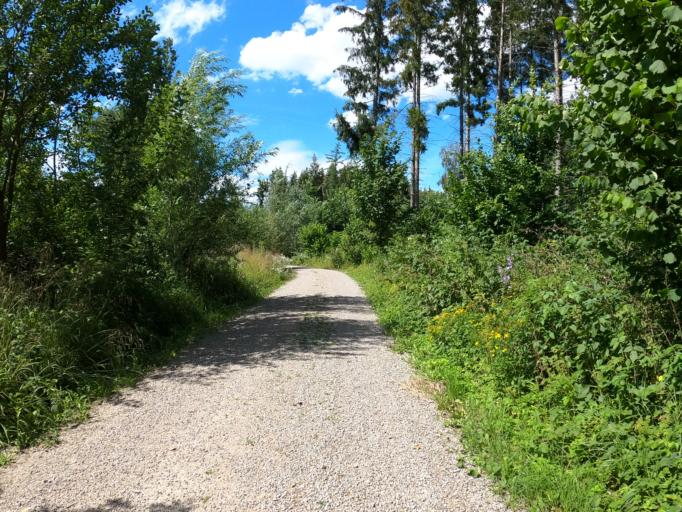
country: DE
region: Bavaria
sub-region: Swabia
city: Leipheim
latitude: 48.4210
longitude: 10.2097
